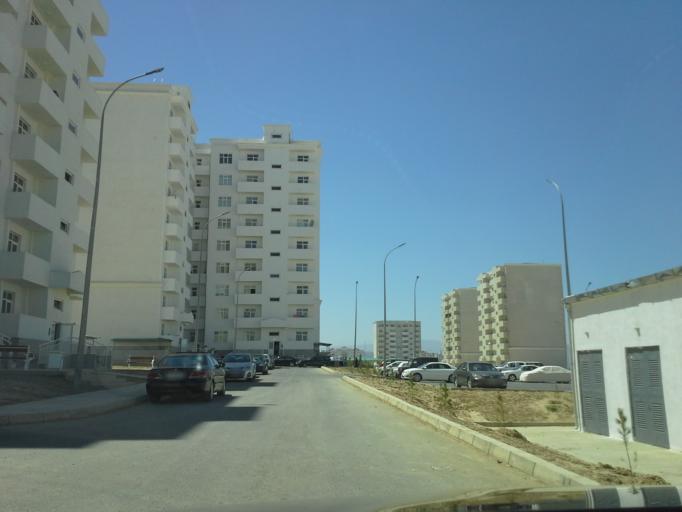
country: TM
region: Ahal
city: Ashgabat
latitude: 37.8860
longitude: 58.4112
